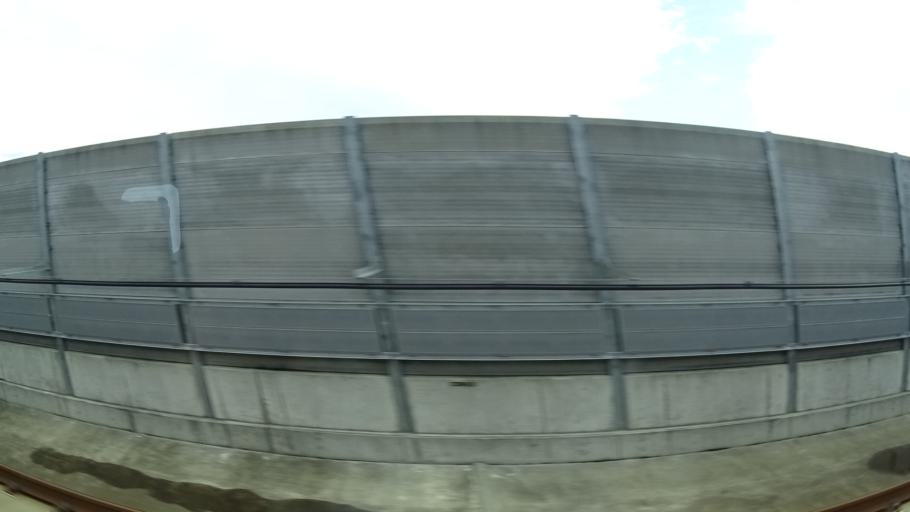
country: JP
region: Toyama
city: Kuragaki-kosugi
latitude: 36.7285
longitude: 137.0959
